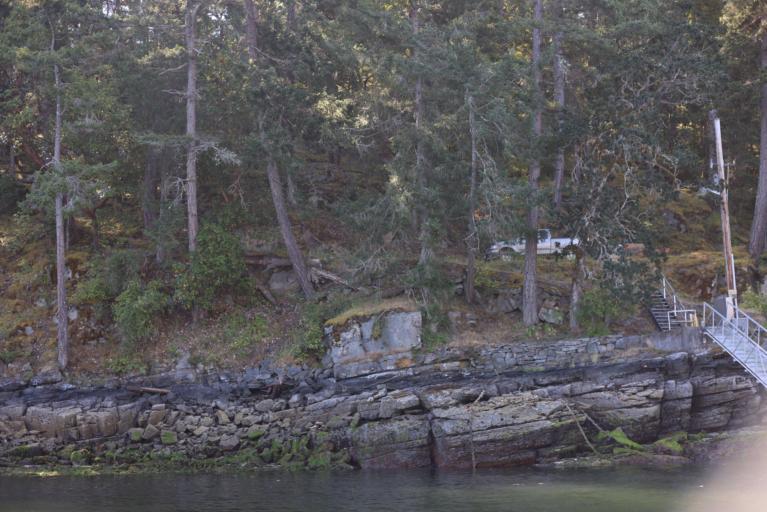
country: CA
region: British Columbia
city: North Cowichan
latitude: 48.7983
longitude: -123.5983
